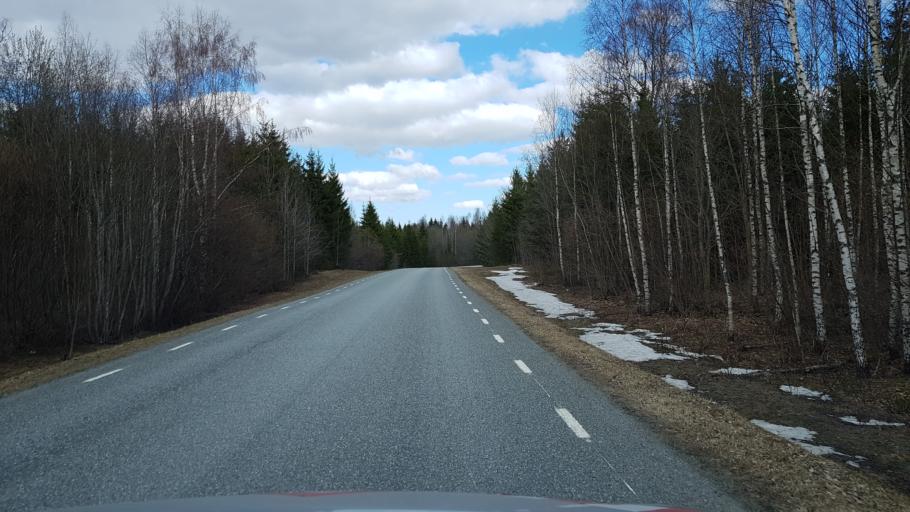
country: EE
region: Laeaene-Virumaa
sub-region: Kadrina vald
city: Kadrina
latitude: 59.2562
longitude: 26.2301
